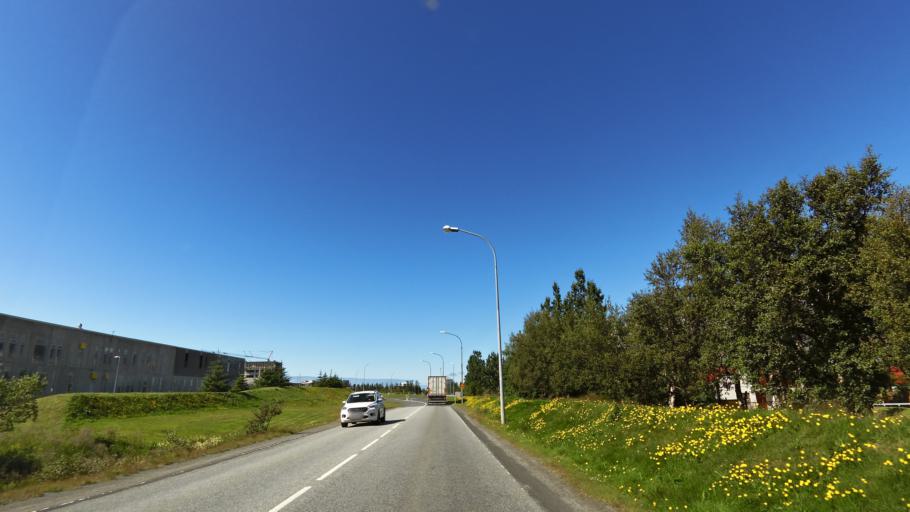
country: IS
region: Capital Region
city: Mosfellsbaer
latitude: 64.1628
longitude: -21.6859
